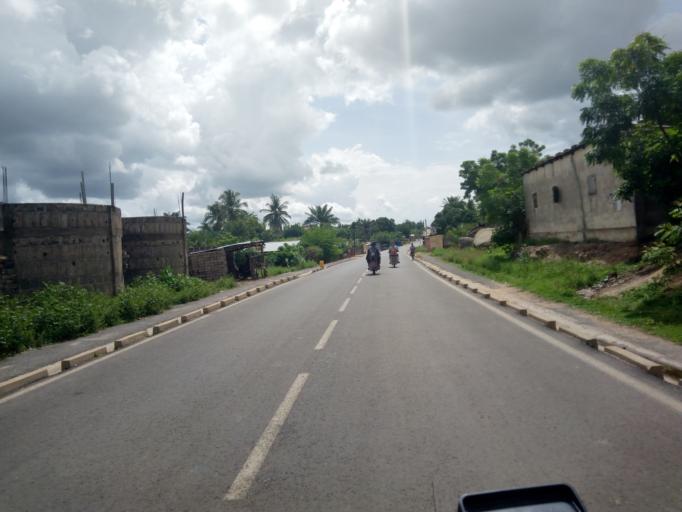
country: TG
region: Kara
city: Kara
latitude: 9.5444
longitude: 1.1804
